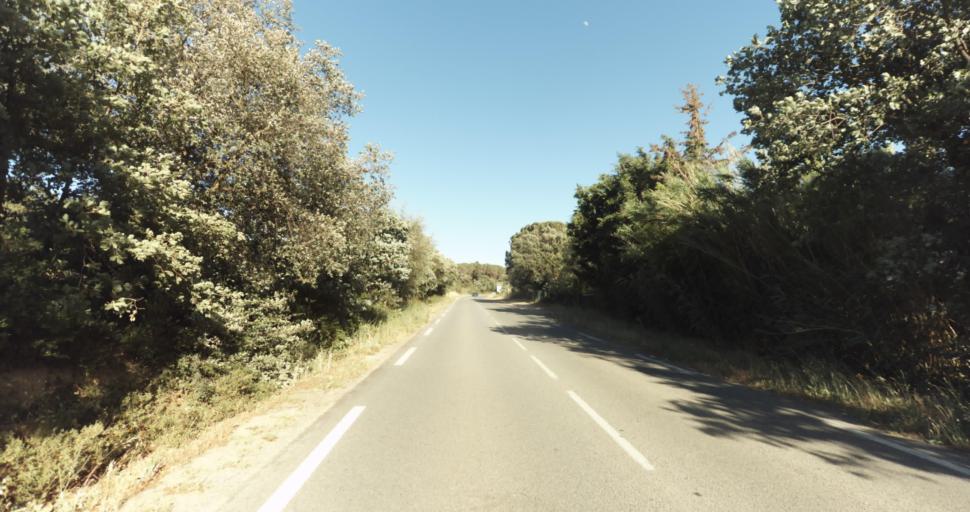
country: FR
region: Provence-Alpes-Cote d'Azur
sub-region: Departement du Var
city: Ramatuelle
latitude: 43.2383
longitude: 6.6060
